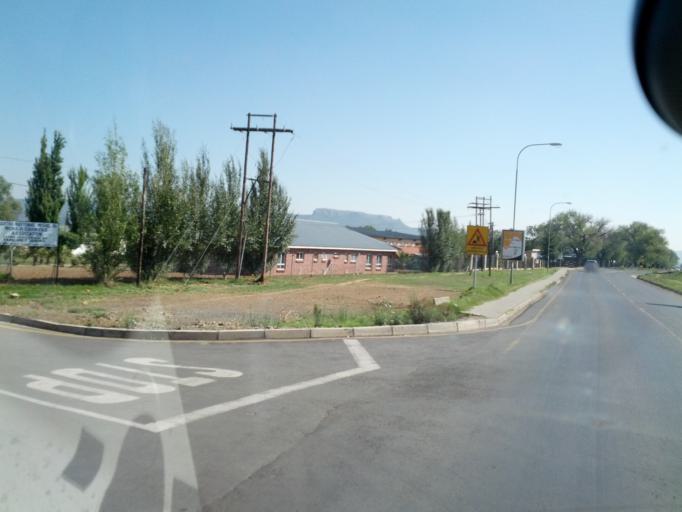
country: LS
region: Maseru
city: Maseru
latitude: -29.3022
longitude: 27.5014
